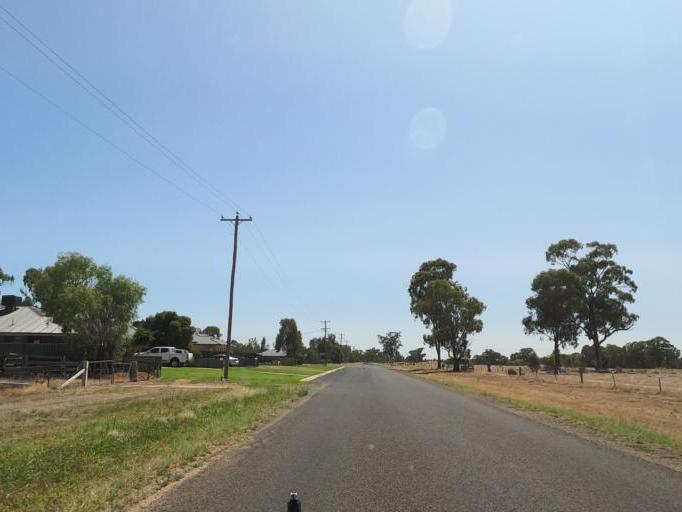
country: AU
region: New South Wales
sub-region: Corowa Shire
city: Mulwala
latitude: -35.9832
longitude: 146.0008
